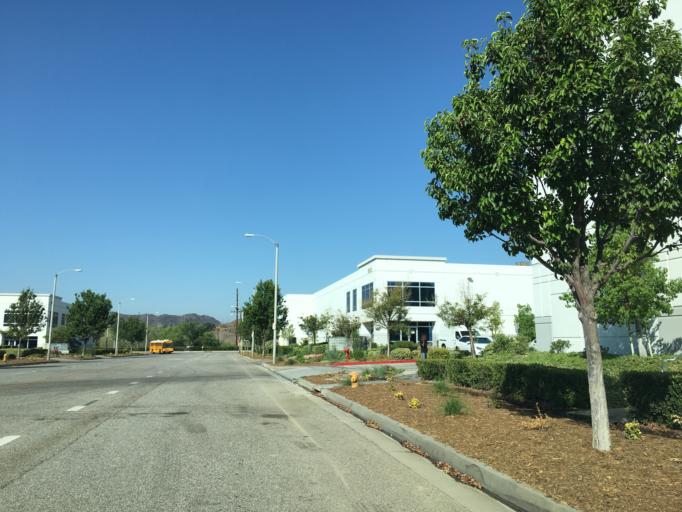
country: US
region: California
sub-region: Los Angeles County
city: Valencia
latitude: 34.4468
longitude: -118.6129
